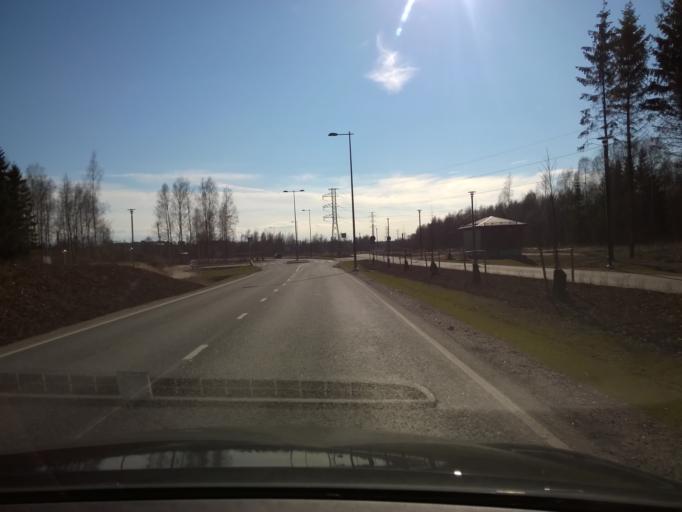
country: FI
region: Uusimaa
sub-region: Helsinki
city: Kilo
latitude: 60.1872
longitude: 24.7775
